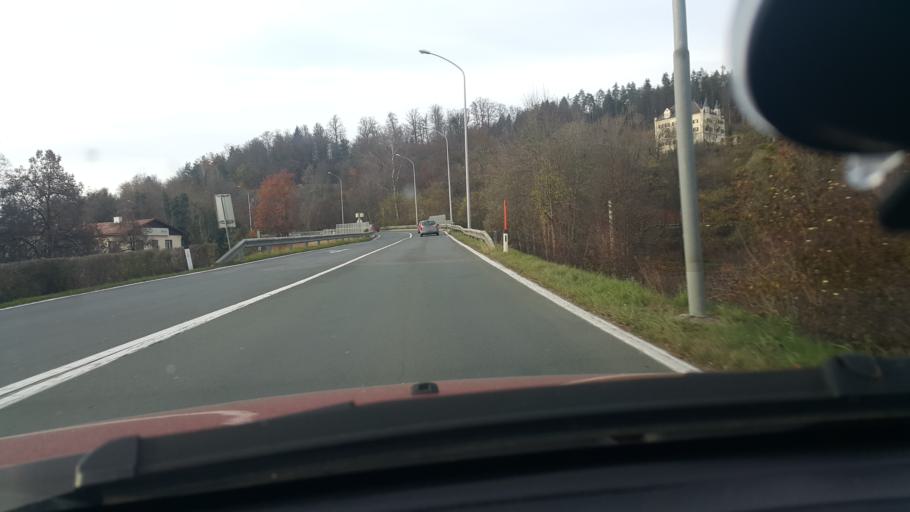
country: AT
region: Carinthia
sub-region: Klagenfurt am Woerthersee
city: Klagenfurt am Woerthersee
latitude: 46.6227
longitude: 14.2584
